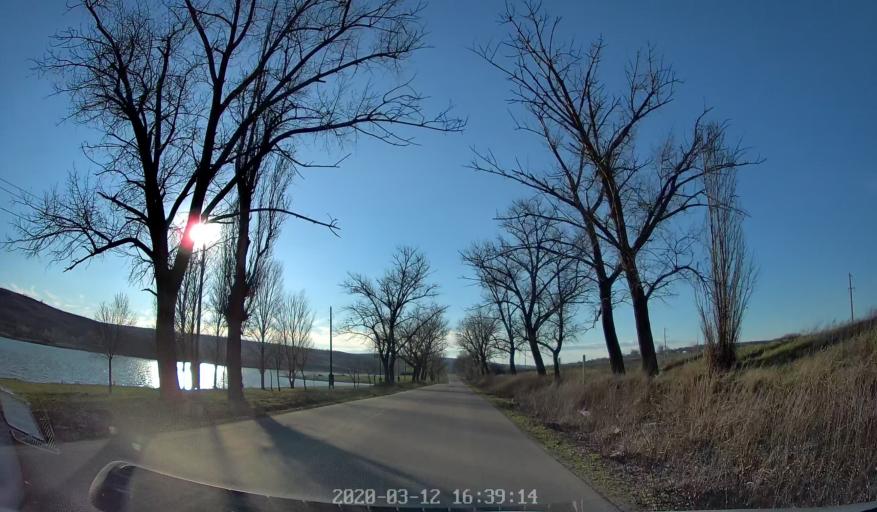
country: MD
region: Anenii Noi
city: Anenii Noi
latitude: 46.8147
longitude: 29.1695
